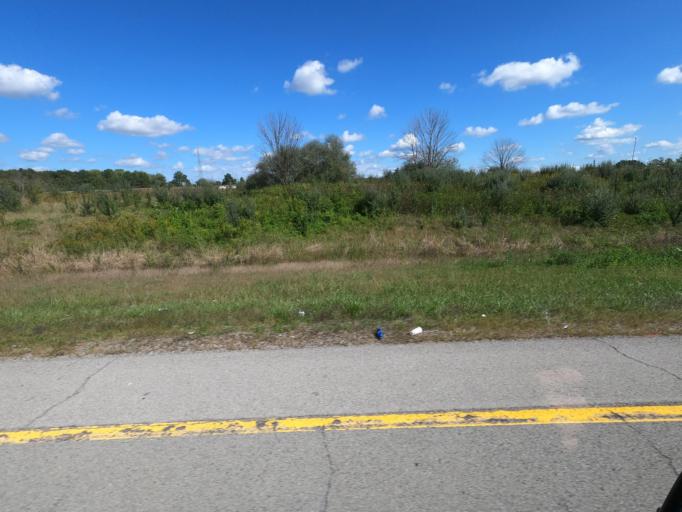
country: US
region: Illinois
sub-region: Jefferson County
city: Mount Vernon
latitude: 38.3612
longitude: -89.0373
